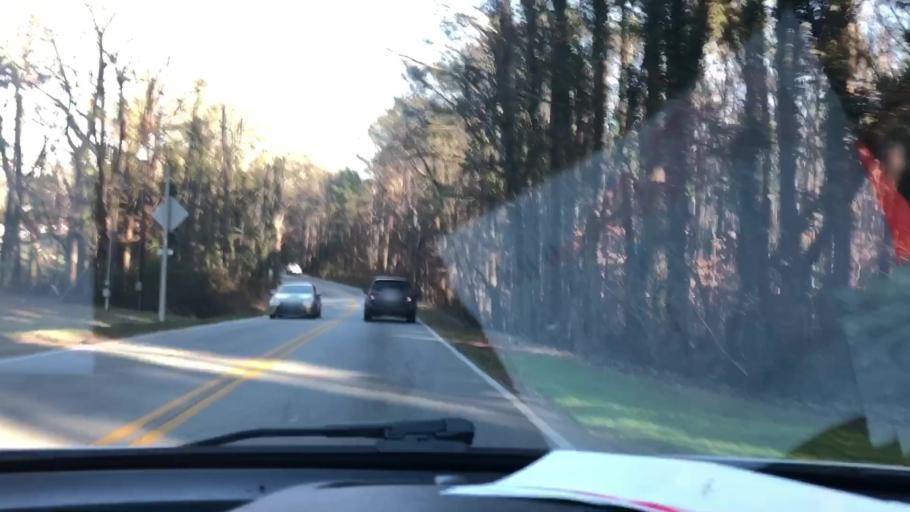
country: US
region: Georgia
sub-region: Gwinnett County
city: Mountain Park
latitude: 33.8298
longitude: -84.1492
